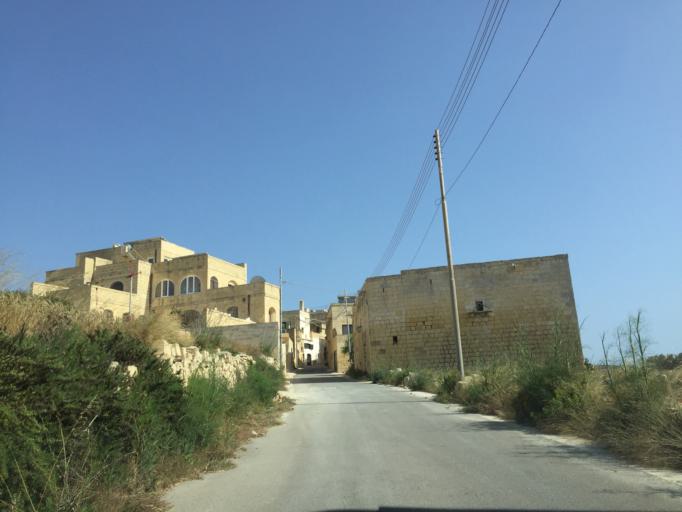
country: MT
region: L-Gharb
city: Gharb
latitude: 36.0651
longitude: 14.2062
